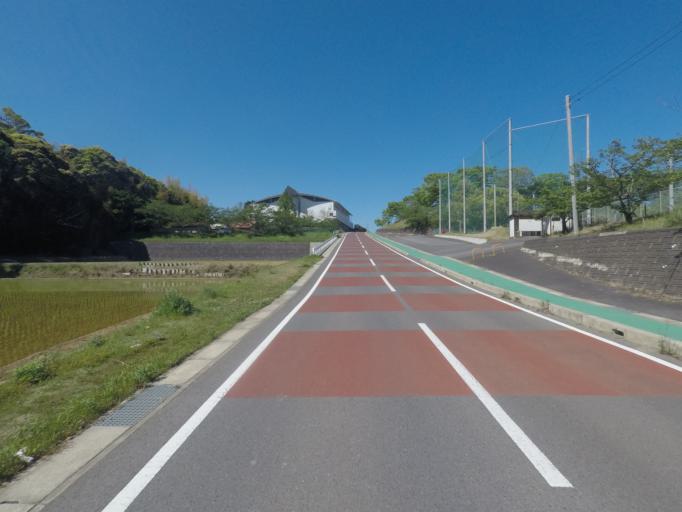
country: JP
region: Ibaraki
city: Itako
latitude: 36.0214
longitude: 140.4747
